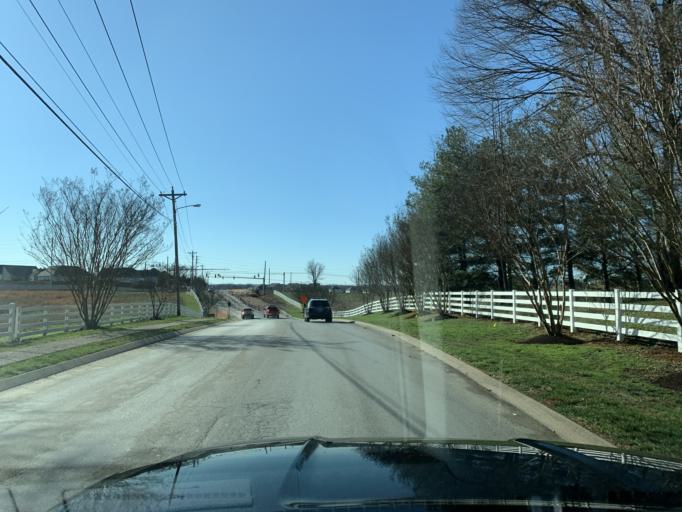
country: US
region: Tennessee
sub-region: Maury County
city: Spring Hill
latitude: 35.7542
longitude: -86.9020
